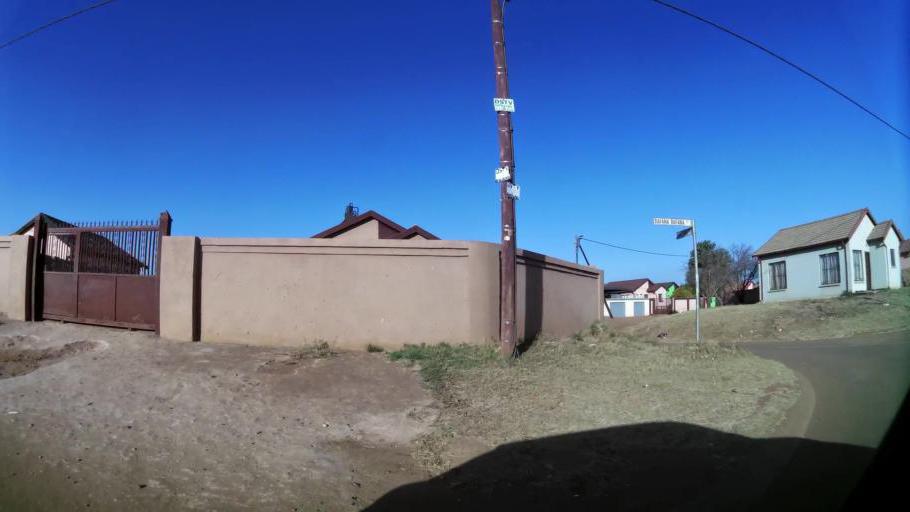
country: ZA
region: Gauteng
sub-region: City of Tshwane Metropolitan Municipality
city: Mabopane
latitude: -25.5944
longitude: 28.1117
